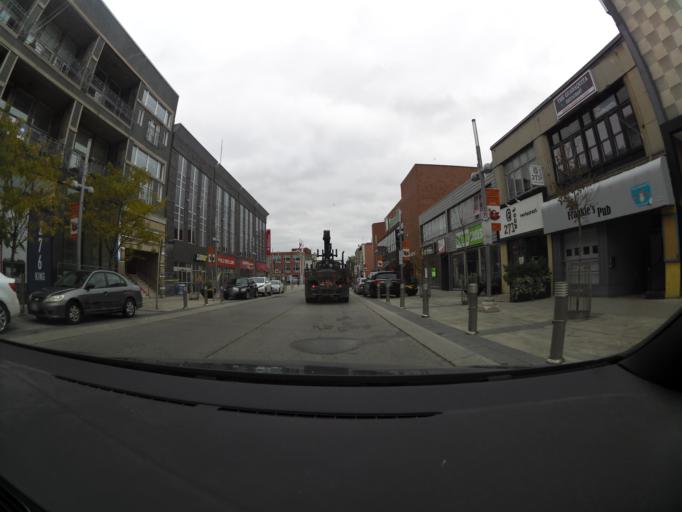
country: CA
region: Ontario
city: Waterloo
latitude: 43.4515
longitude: -80.4943
